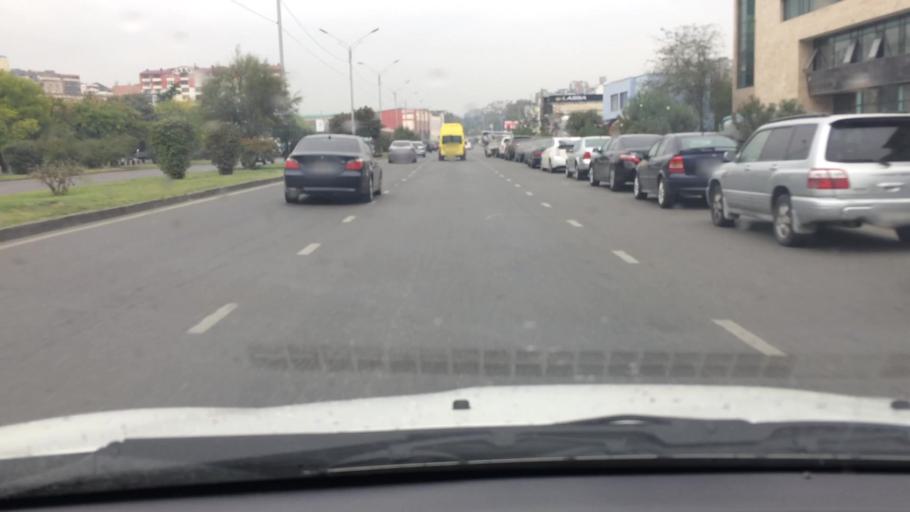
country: GE
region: T'bilisi
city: Tbilisi
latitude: 41.6787
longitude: 44.8286
